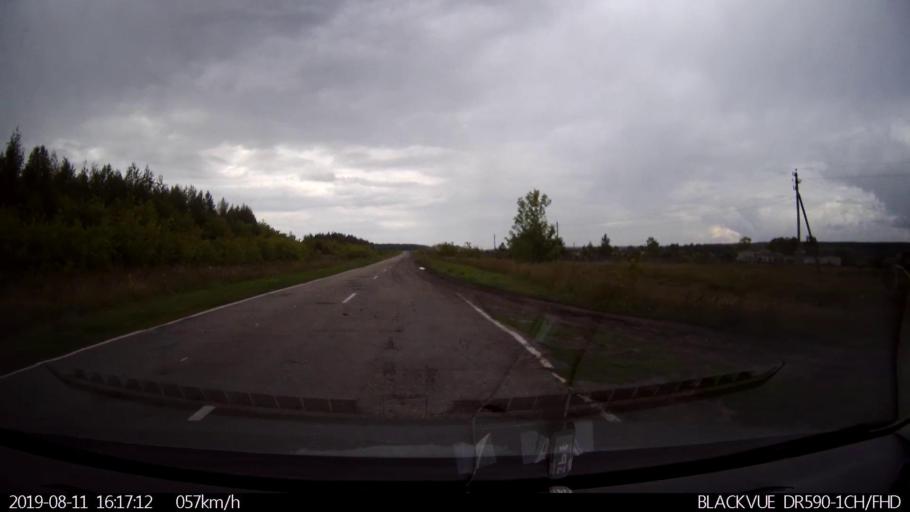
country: RU
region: Ulyanovsk
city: Mayna
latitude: 54.0467
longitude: 47.6172
